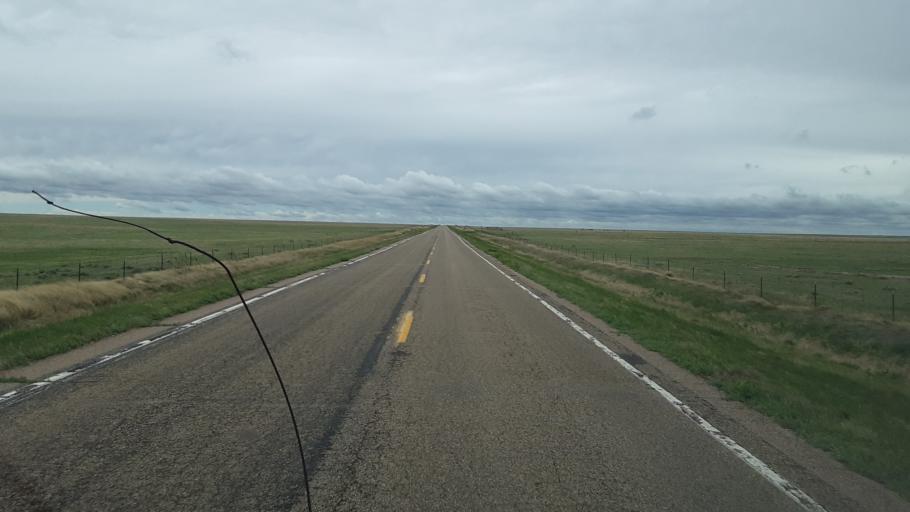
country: US
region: Colorado
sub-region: Lincoln County
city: Hugo
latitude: 38.8521
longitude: -103.7534
